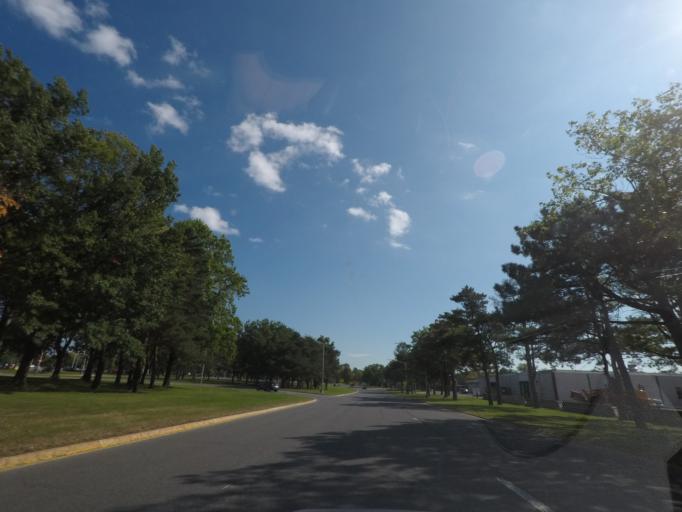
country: US
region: New York
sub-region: Albany County
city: Roessleville
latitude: 42.6753
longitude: -73.8104
